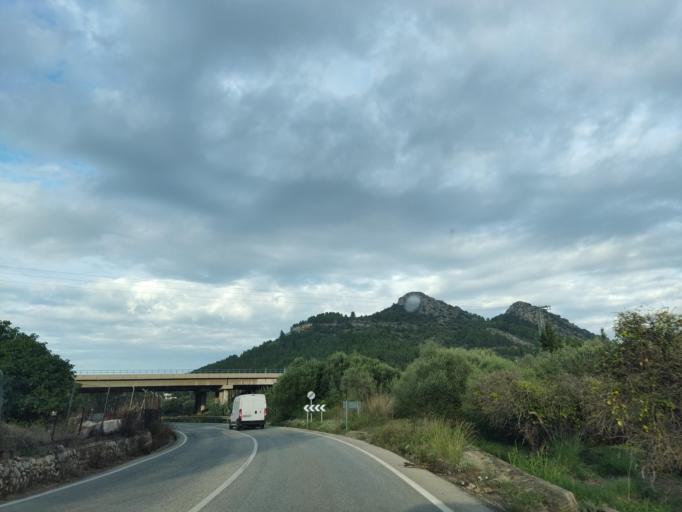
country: ES
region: Valencia
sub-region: Provincia de Alicante
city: Pedreguer
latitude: 38.8031
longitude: 0.0330
